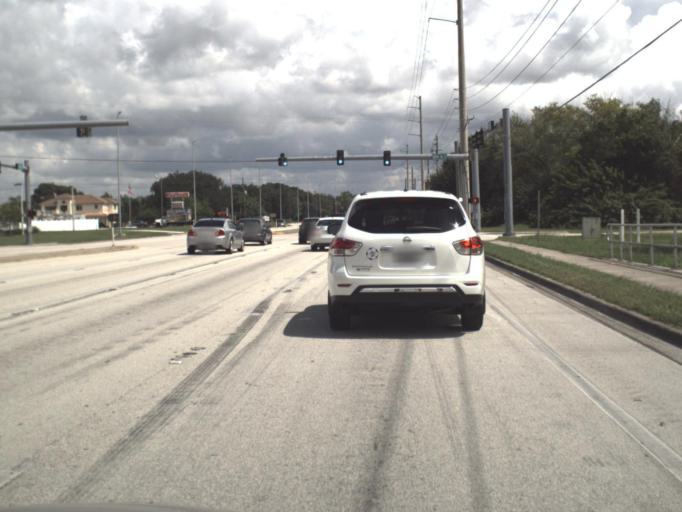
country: US
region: Florida
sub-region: Manatee County
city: Samoset
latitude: 27.4472
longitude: -82.5168
